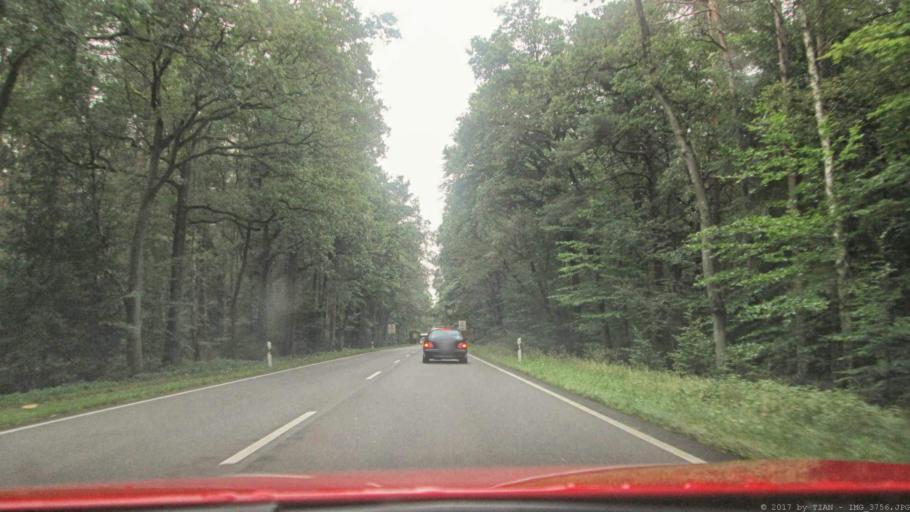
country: DE
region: Lower Saxony
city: Suderburg
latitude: 52.8830
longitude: 10.5032
